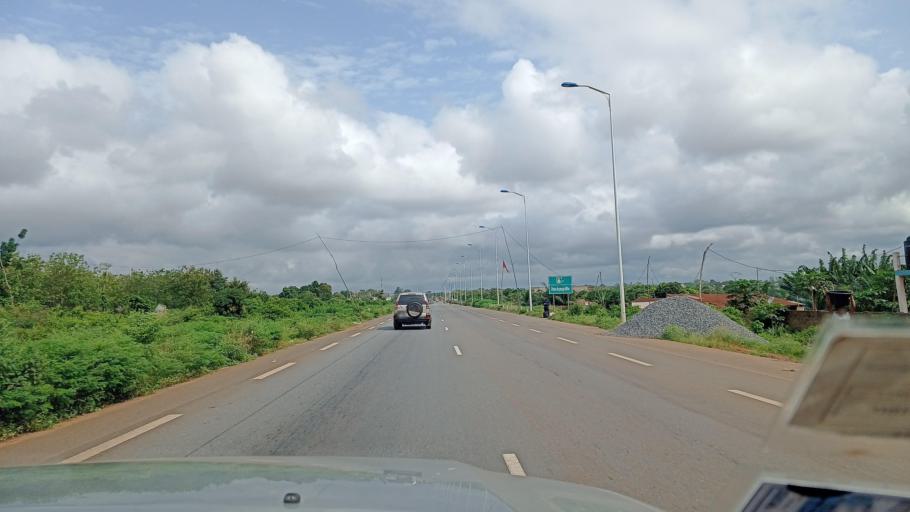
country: TG
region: Maritime
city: Tsevie
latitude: 6.3669
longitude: 1.2079
